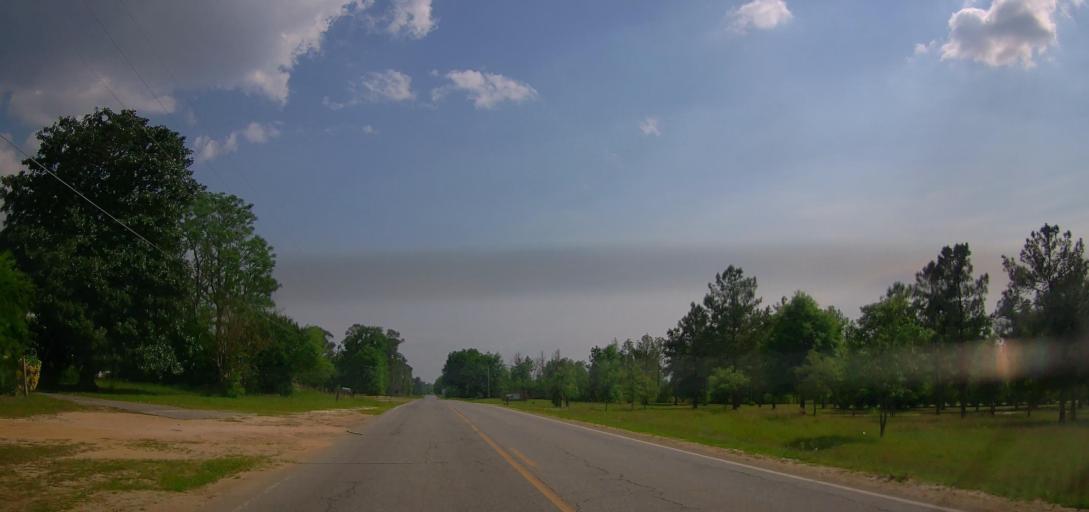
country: US
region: Georgia
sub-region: Laurens County
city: East Dublin
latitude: 32.5910
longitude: -82.8652
